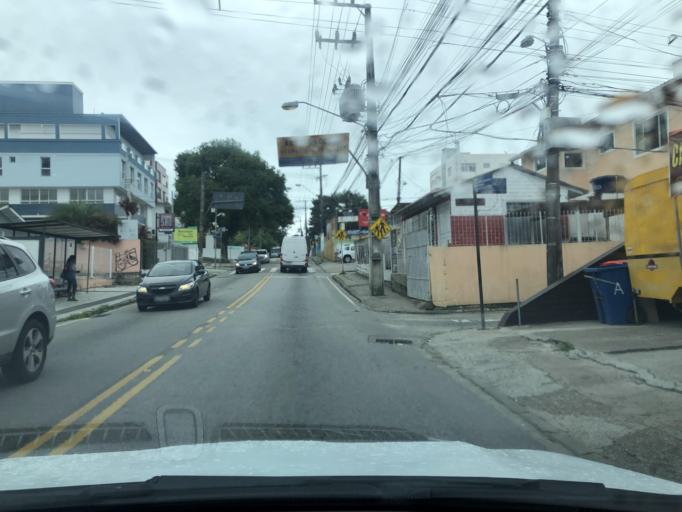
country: BR
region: Santa Catarina
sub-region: Florianopolis
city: Pantanal
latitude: -27.6097
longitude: -48.5228
